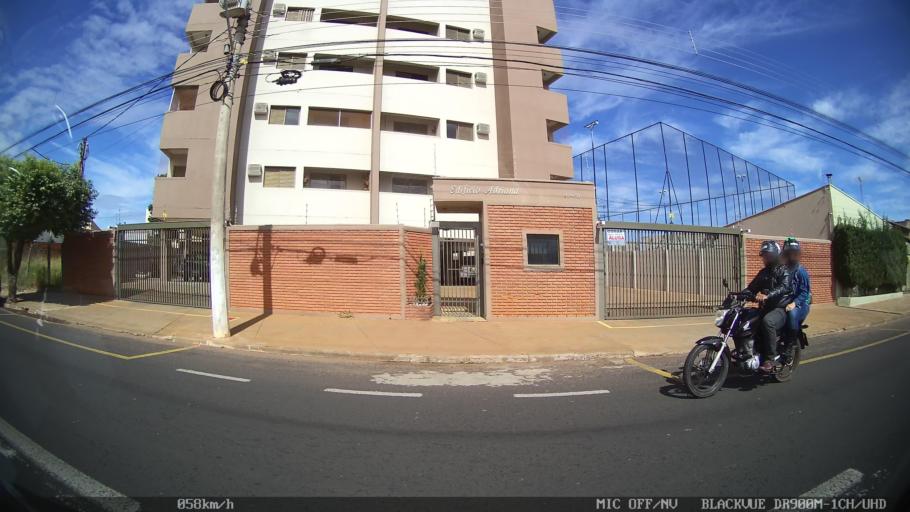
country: BR
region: Sao Paulo
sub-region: Bady Bassitt
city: Bady Bassitt
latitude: -20.8134
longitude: -49.5009
